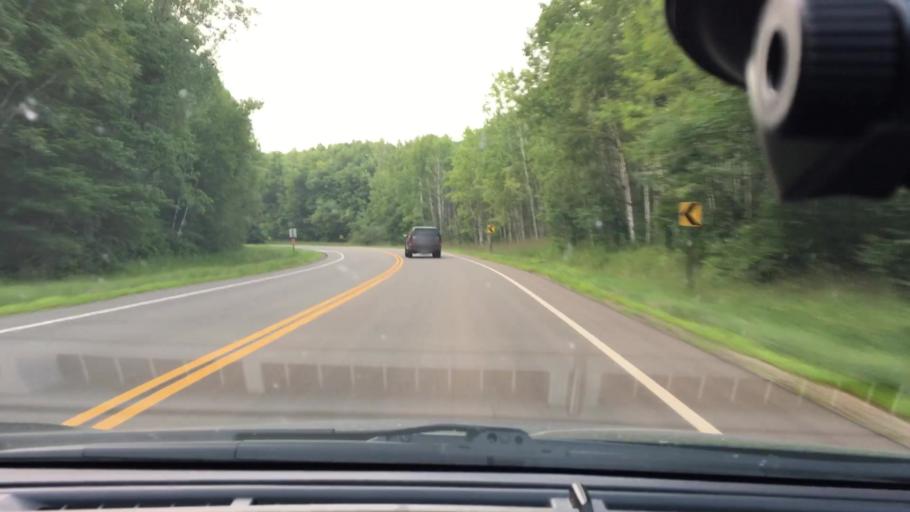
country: US
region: Minnesota
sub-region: Crow Wing County
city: Crosby
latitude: 46.5221
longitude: -93.9245
